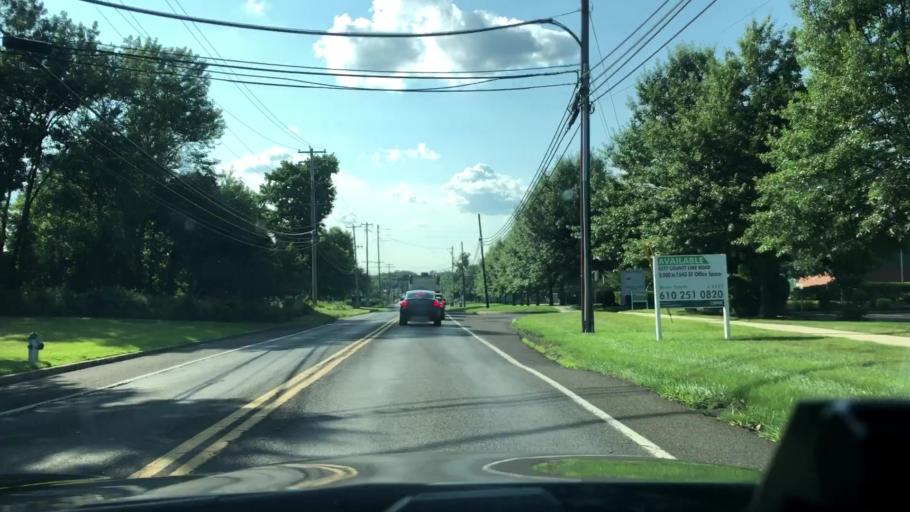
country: US
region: Pennsylvania
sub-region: Montgomery County
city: Montgomeryville
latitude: 40.2742
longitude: -75.2428
